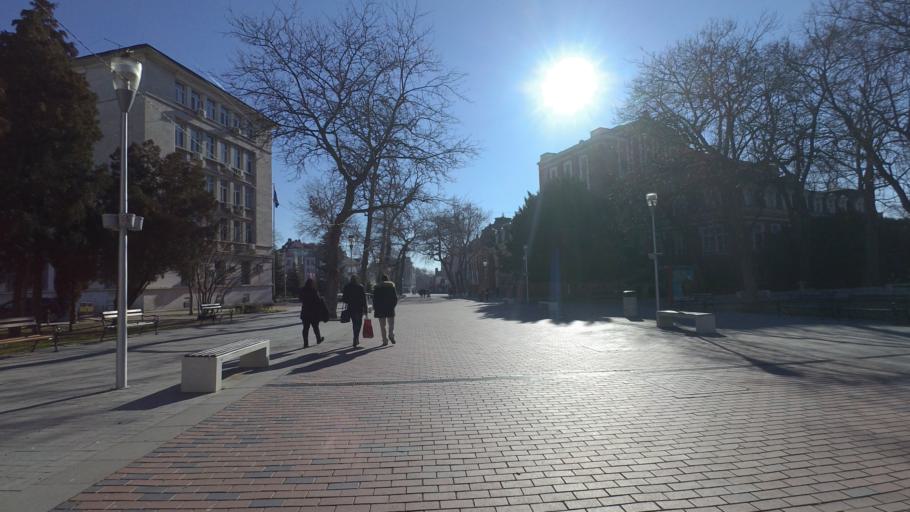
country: BG
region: Varna
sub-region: Obshtina Varna
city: Varna
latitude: 43.2043
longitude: 27.9113
